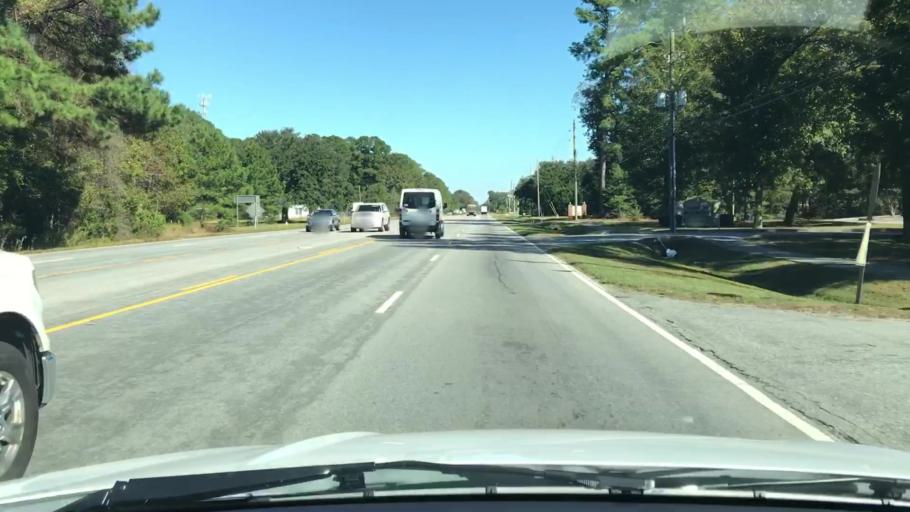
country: US
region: South Carolina
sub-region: Charleston County
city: Ravenel
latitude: 32.7768
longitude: -80.2451
